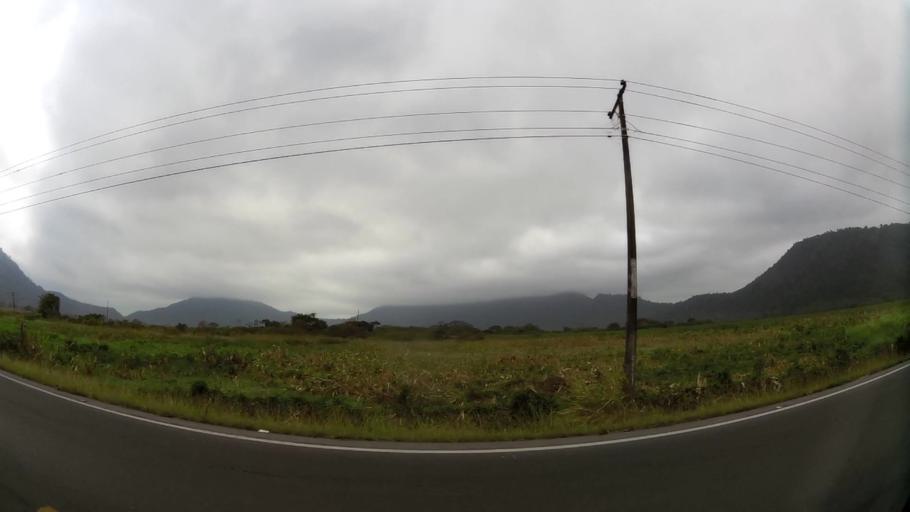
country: EC
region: Guayas
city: Naranjal
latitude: -2.4310
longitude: -79.6261
